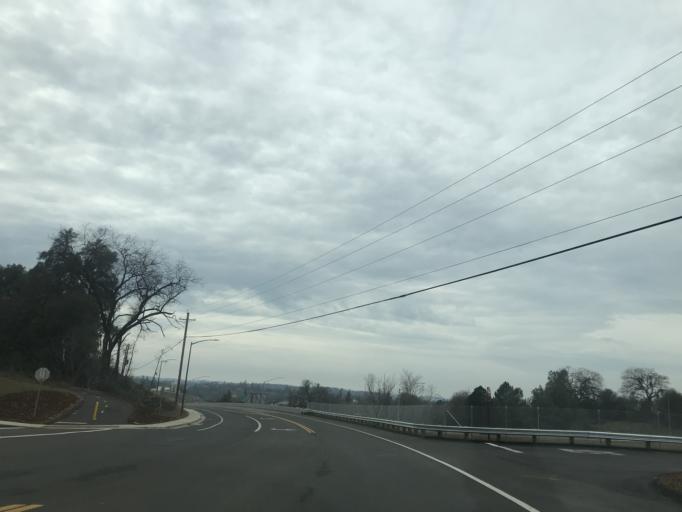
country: US
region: California
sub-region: El Dorado County
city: Placerville
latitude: 38.7254
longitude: -120.8255
